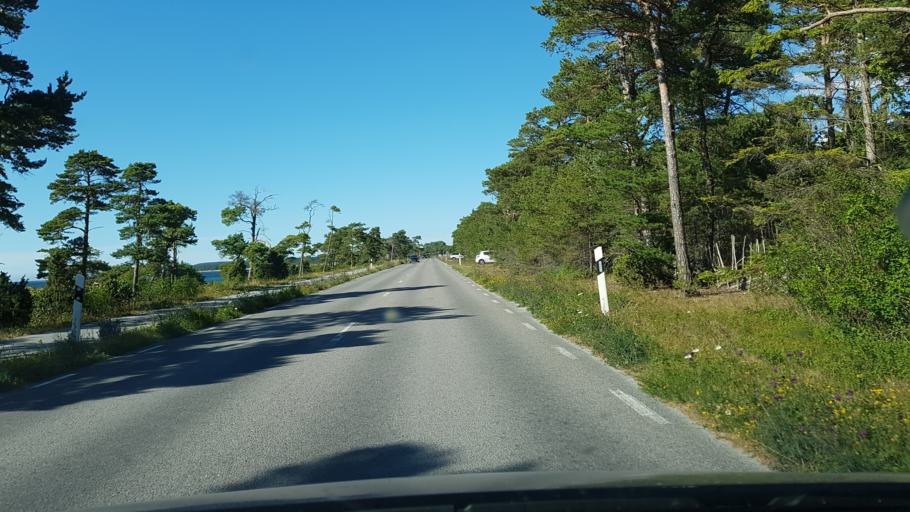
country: SE
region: Gotland
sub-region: Gotland
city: Klintehamn
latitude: 57.4761
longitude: 18.1246
